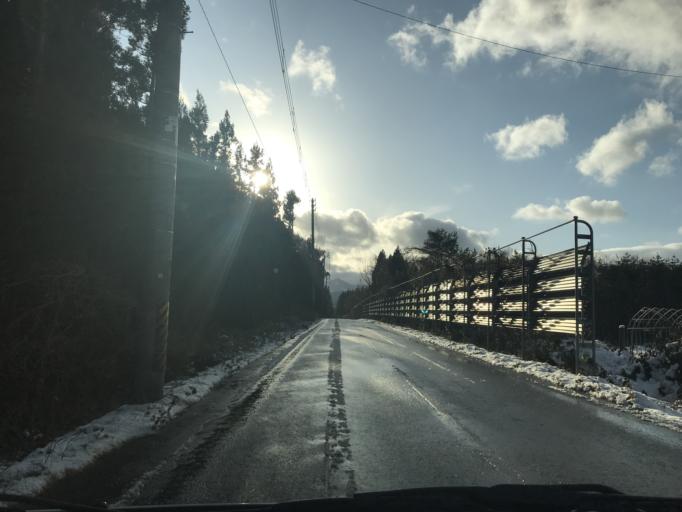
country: JP
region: Iwate
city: Kitakami
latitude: 39.2491
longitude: 141.0118
